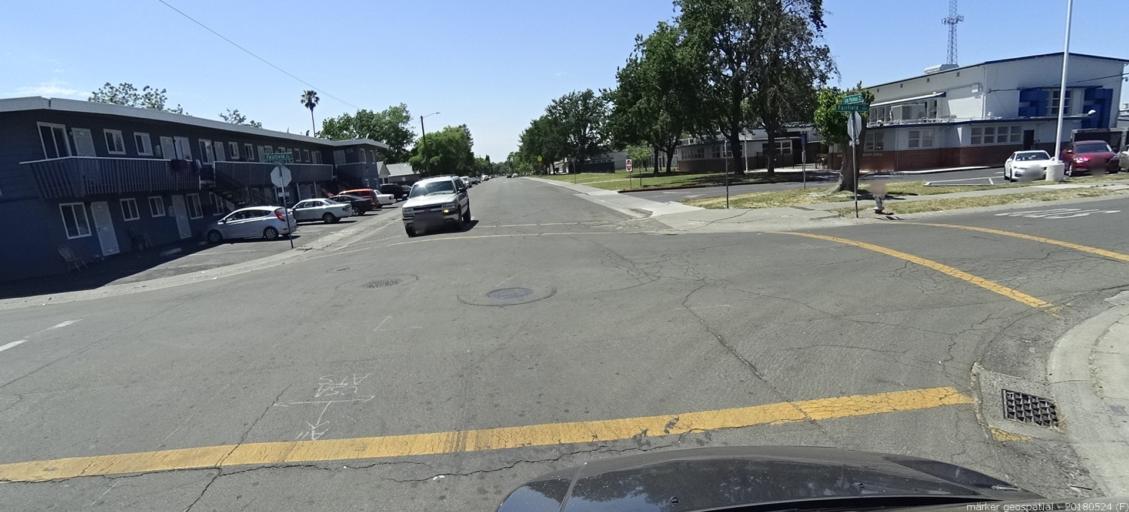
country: US
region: California
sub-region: Sacramento County
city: Sacramento
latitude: 38.6187
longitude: -121.4522
